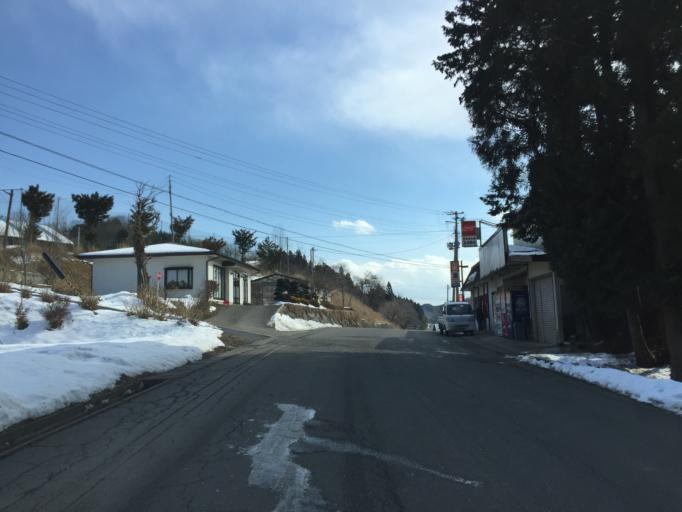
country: JP
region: Fukushima
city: Ishikawa
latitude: 37.1988
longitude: 140.5335
